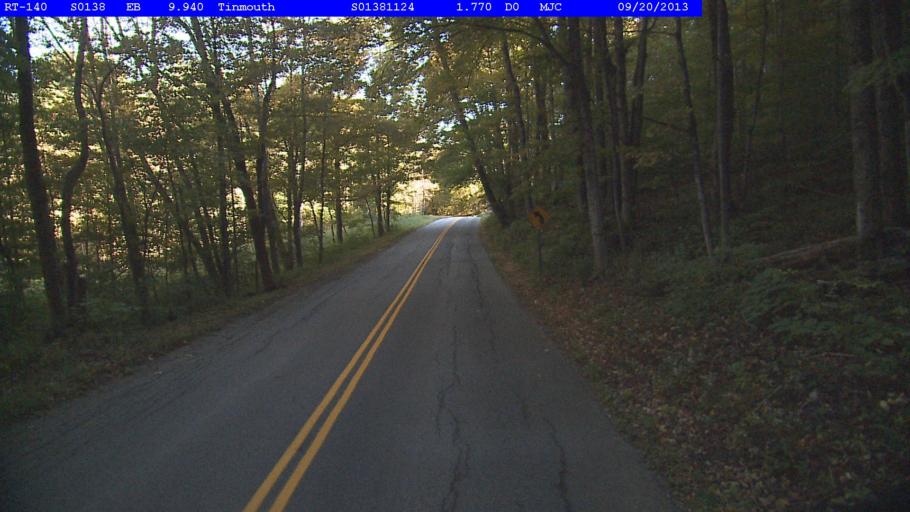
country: US
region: Vermont
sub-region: Rutland County
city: West Rutland
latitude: 43.4691
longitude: -73.0496
